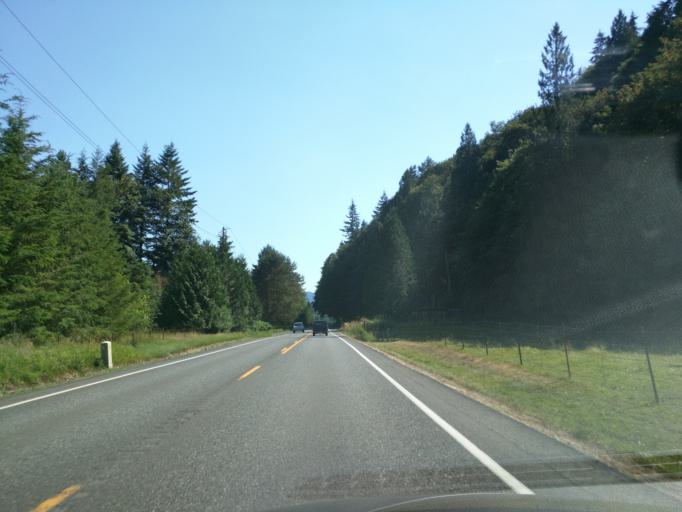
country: US
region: Washington
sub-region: Whatcom County
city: Peaceful Valley
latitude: 48.8561
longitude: -122.1546
